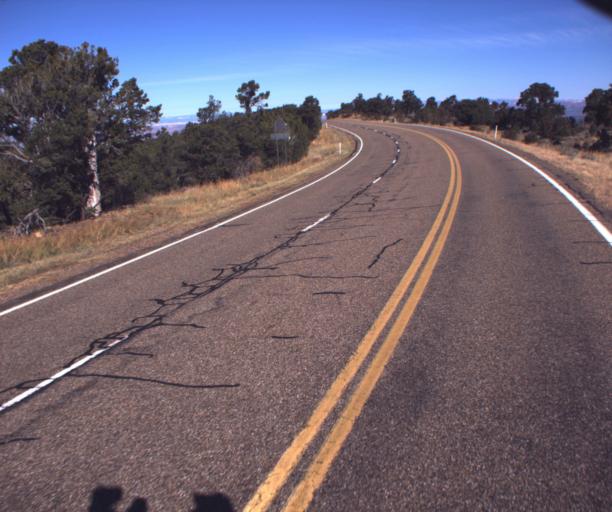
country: US
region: Arizona
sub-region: Coconino County
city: Fredonia
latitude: 36.8013
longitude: -112.2534
